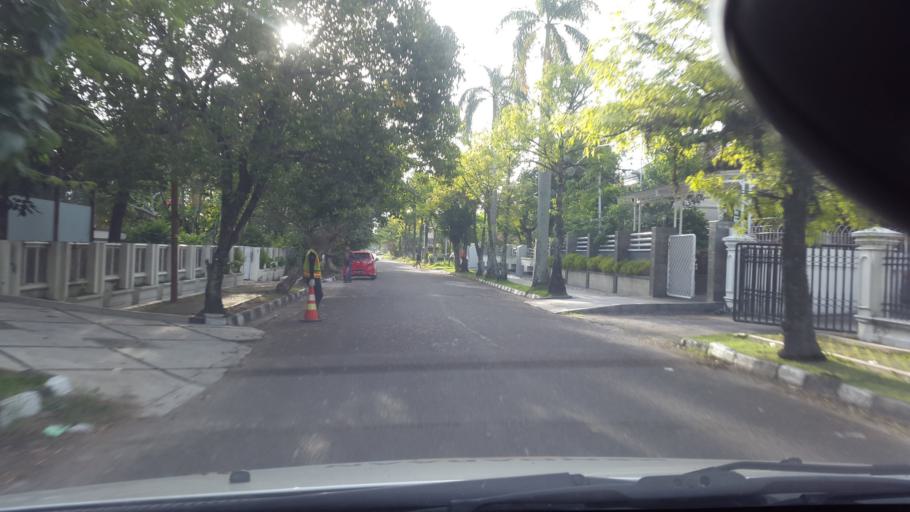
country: ID
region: West Sumatra
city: Padang
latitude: -0.9274
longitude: 100.3562
